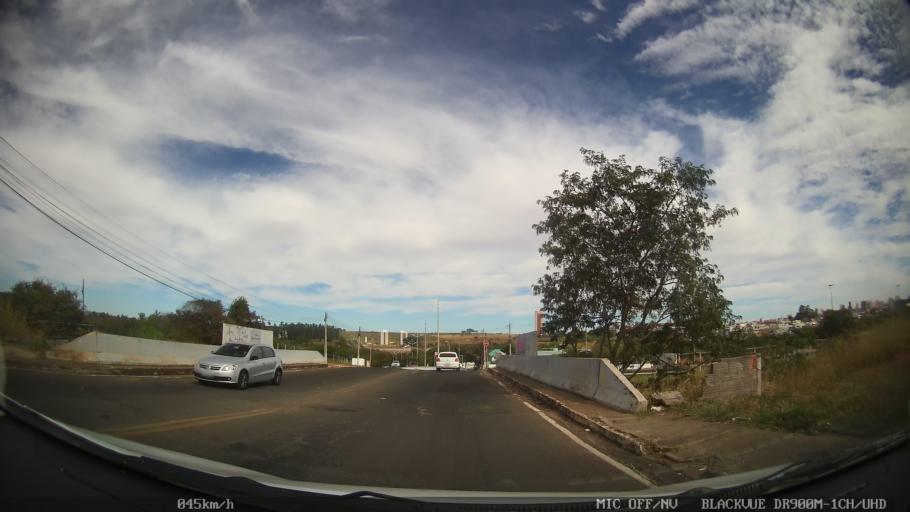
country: BR
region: Sao Paulo
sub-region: Catanduva
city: Catanduva
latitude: -21.1479
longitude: -48.9484
